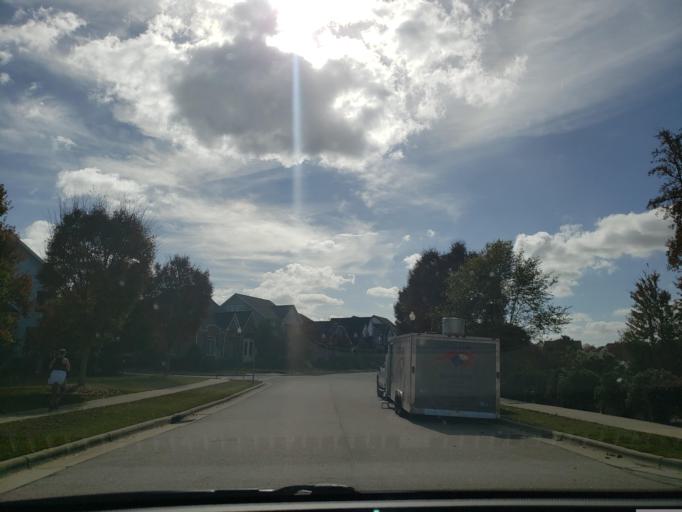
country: US
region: North Carolina
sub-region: Wake County
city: Apex
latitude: 35.7465
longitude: -78.8437
